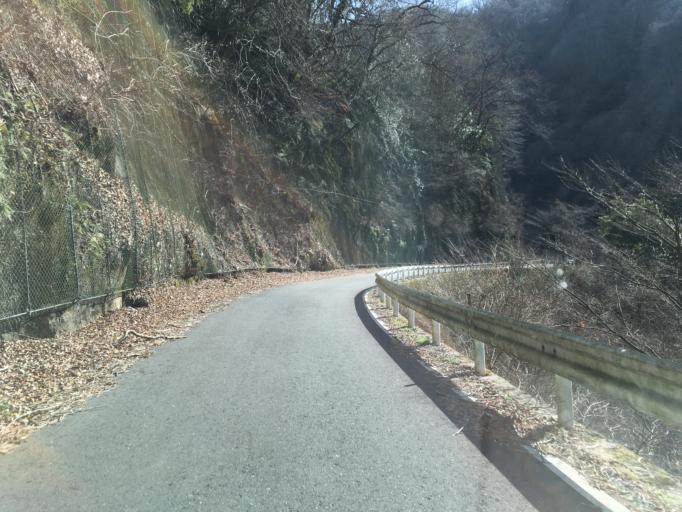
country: JP
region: Ibaraki
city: Kitaibaraki
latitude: 36.7861
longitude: 140.6638
